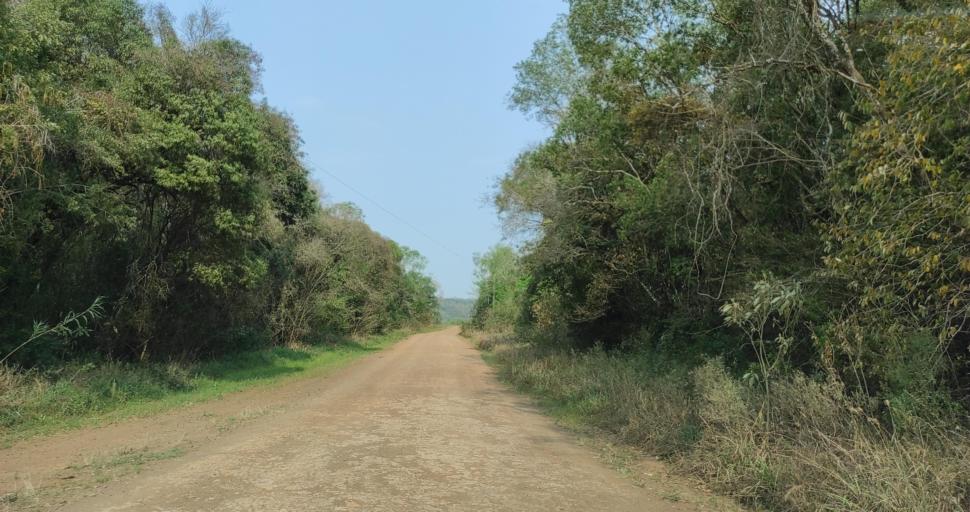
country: AR
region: Misiones
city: Cerro Cora
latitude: -27.5464
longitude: -55.5834
